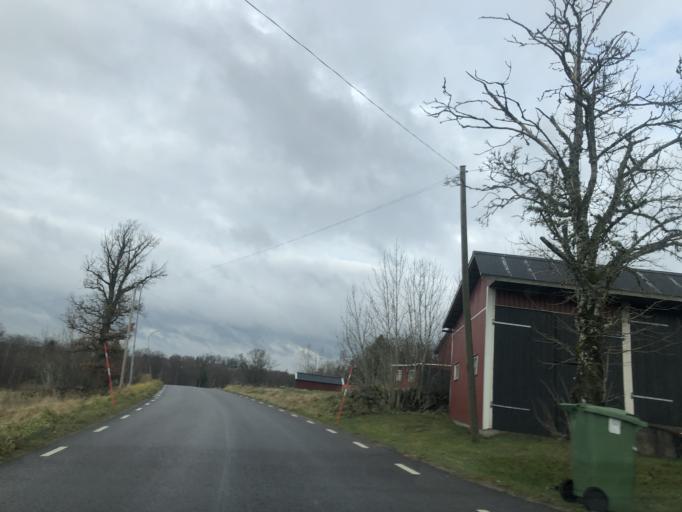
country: SE
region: Vaestra Goetaland
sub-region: Ulricehamns Kommun
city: Ulricehamn
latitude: 57.8169
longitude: 13.2444
